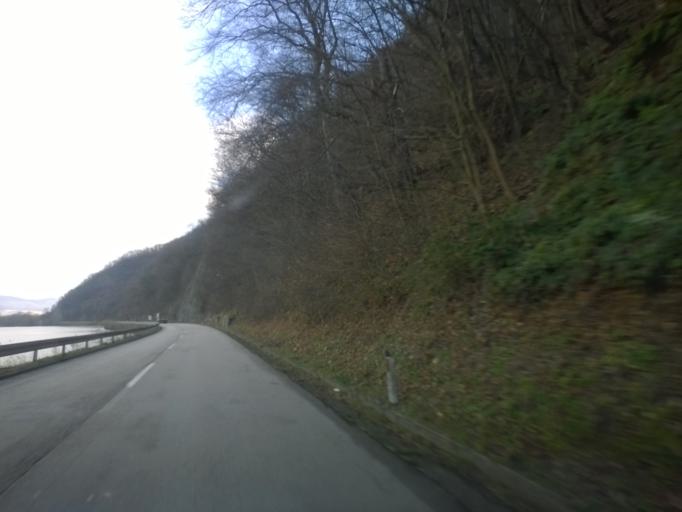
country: RO
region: Caras-Severin
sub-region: Comuna Berzasca
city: Liubcova
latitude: 44.6444
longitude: 21.8250
